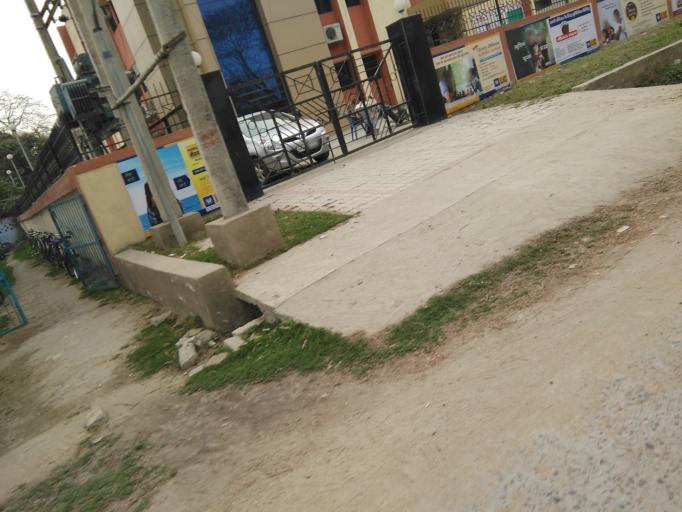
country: IN
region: Bihar
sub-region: Muzaffarpur
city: Muzaffarpur
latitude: 26.1008
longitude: 85.4089
